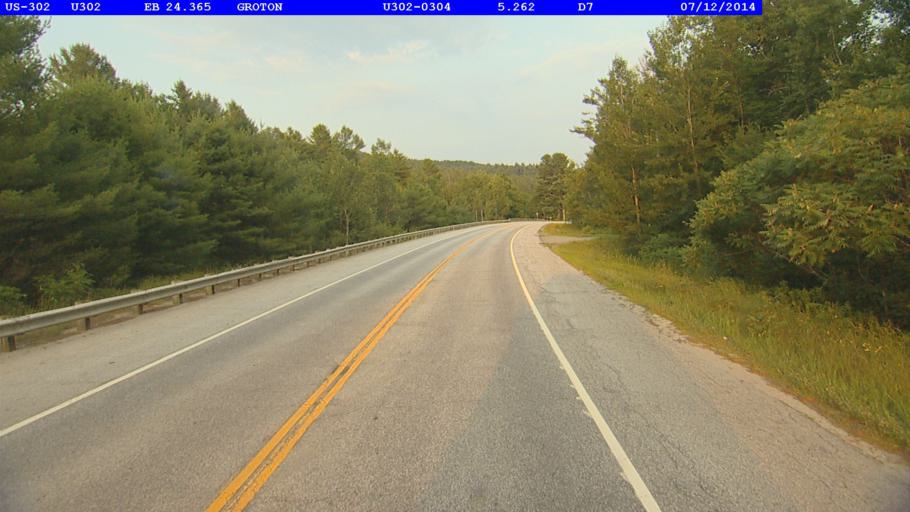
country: US
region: New Hampshire
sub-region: Grafton County
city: Woodsville
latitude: 44.2194
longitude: -72.2167
